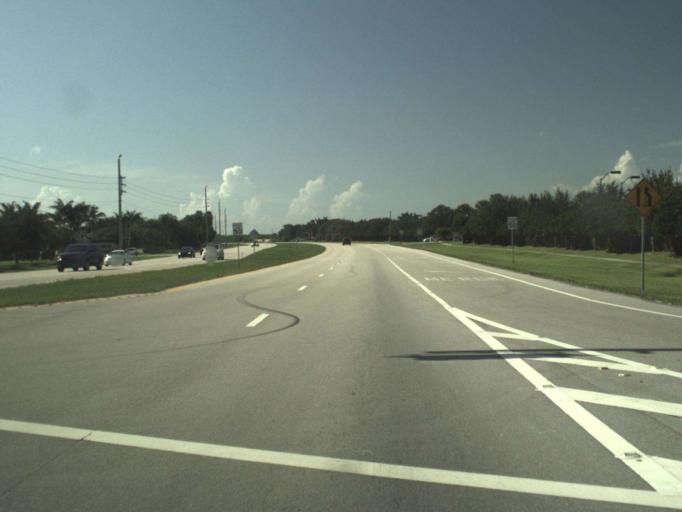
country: US
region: Florida
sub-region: Indian River County
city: Gifford
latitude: 27.6749
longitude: -80.4003
